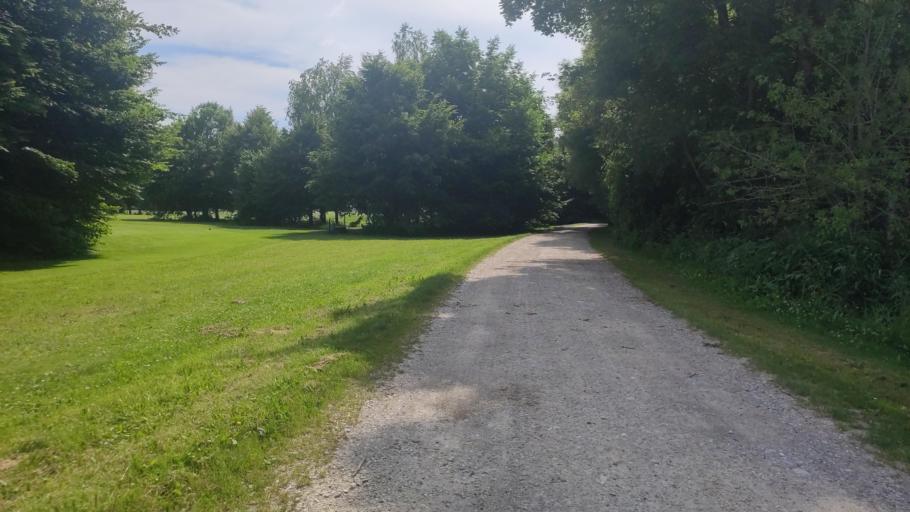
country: DE
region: Bavaria
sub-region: Swabia
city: Konigsbrunn
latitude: 48.2425
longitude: 10.8900
